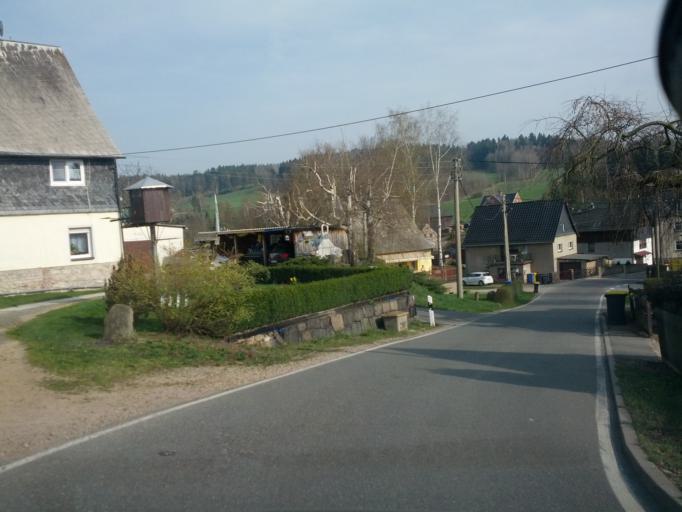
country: DE
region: Saxony
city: Stutzengrun
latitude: 50.5692
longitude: 12.5285
